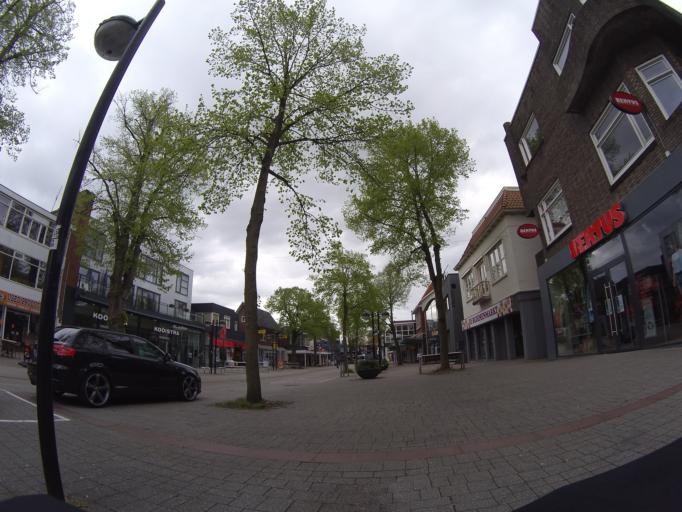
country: NL
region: Drenthe
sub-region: Gemeente Emmen
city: Emmen
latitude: 52.7881
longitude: 6.8946
